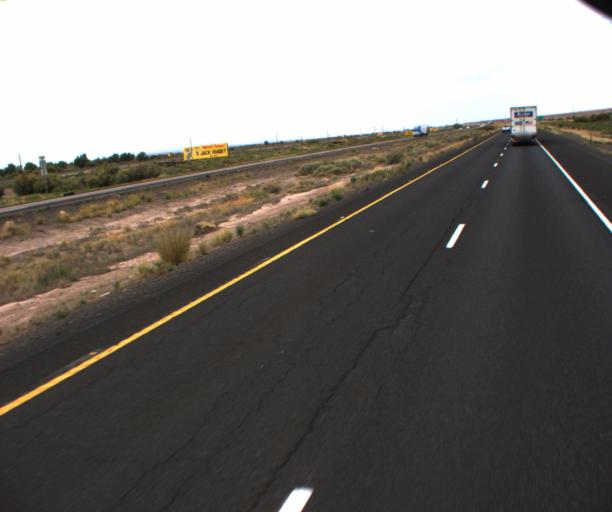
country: US
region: Arizona
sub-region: Navajo County
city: Joseph City
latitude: 34.9678
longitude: -110.4233
